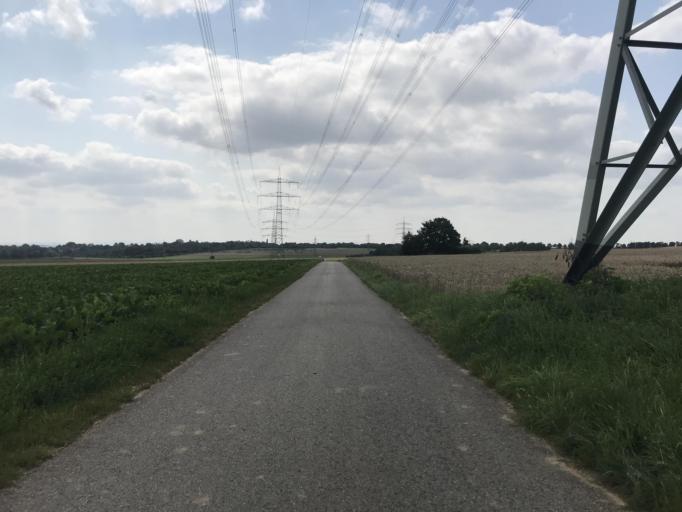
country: DE
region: Hesse
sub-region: Regierungsbezirk Darmstadt
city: Bischofsheim
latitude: 50.0172
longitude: 8.3777
